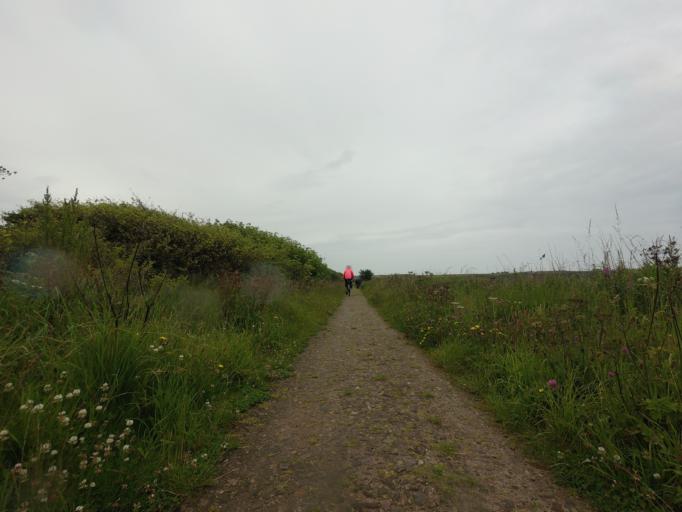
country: GB
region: Scotland
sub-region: Moray
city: Cullen
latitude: 57.6929
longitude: -2.8345
